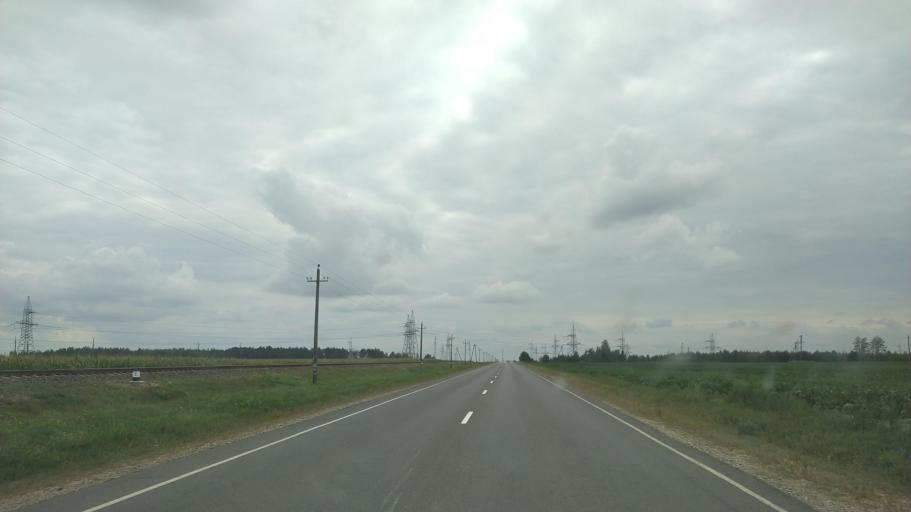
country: BY
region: Brest
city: Byelaazyorsk
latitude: 52.5198
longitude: 25.1511
